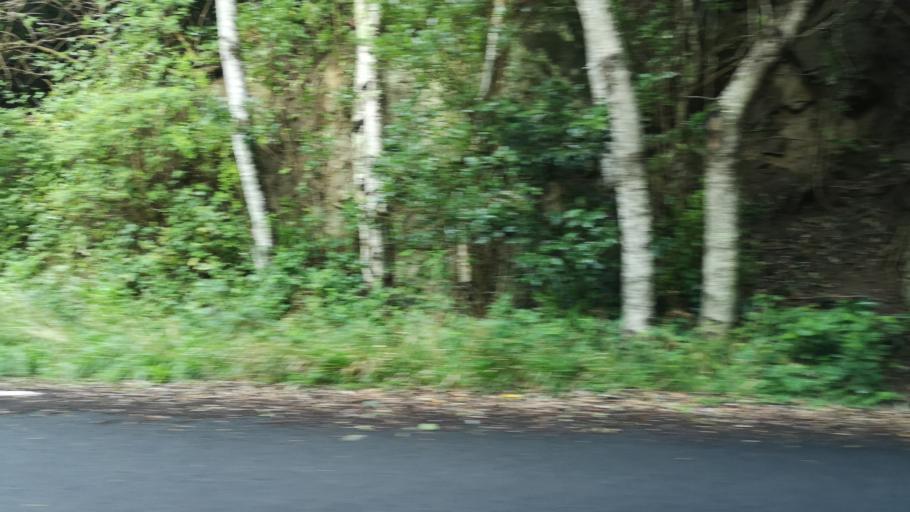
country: ES
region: Canary Islands
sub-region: Provincia de Santa Cruz de Tenerife
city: Hermigua
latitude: 28.1277
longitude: -17.2097
